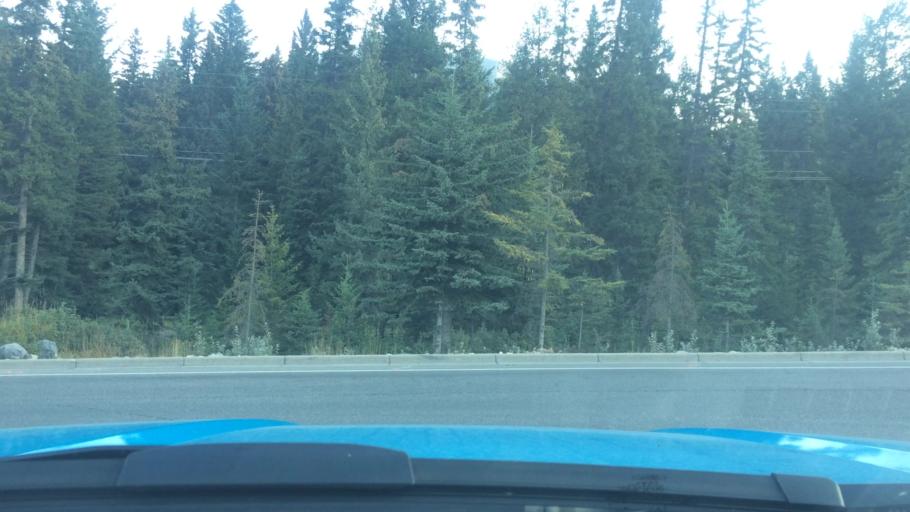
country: CA
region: Alberta
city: Canmore
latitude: 51.0870
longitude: -115.3309
